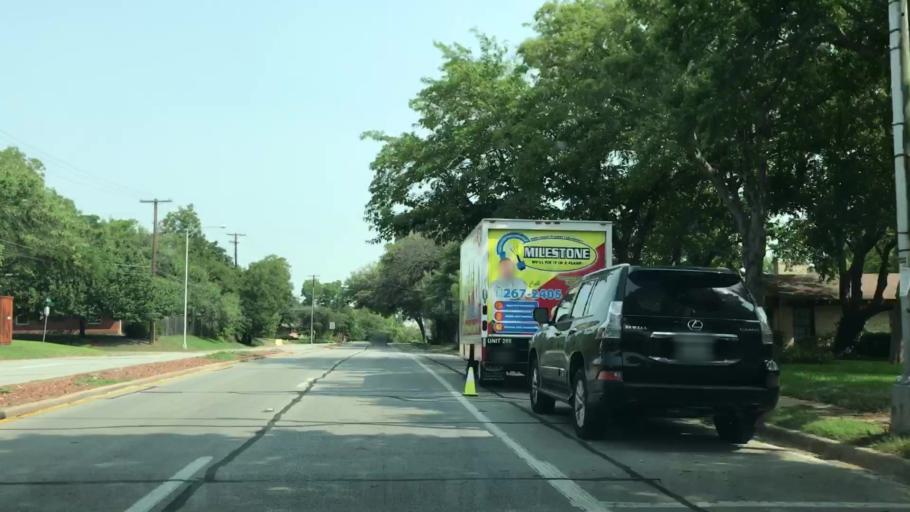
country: US
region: Texas
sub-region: Dallas County
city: Dallas
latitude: 32.7625
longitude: -96.8357
